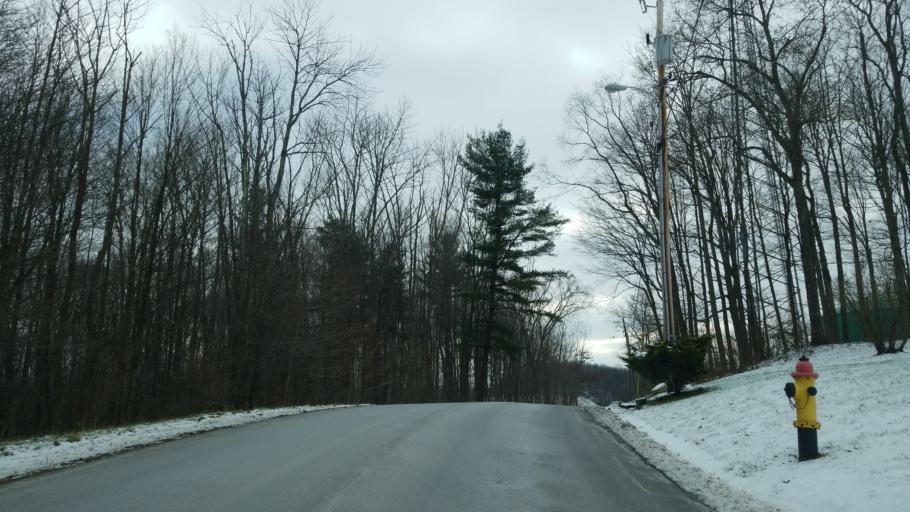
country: US
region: Pennsylvania
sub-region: Clearfield County
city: Sandy
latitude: 41.1040
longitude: -78.7598
